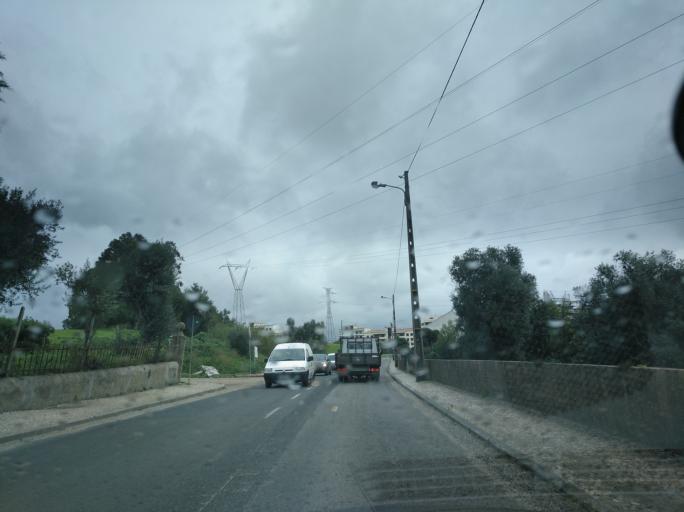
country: PT
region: Lisbon
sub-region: Odivelas
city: Famoes
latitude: 38.7909
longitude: -9.1988
